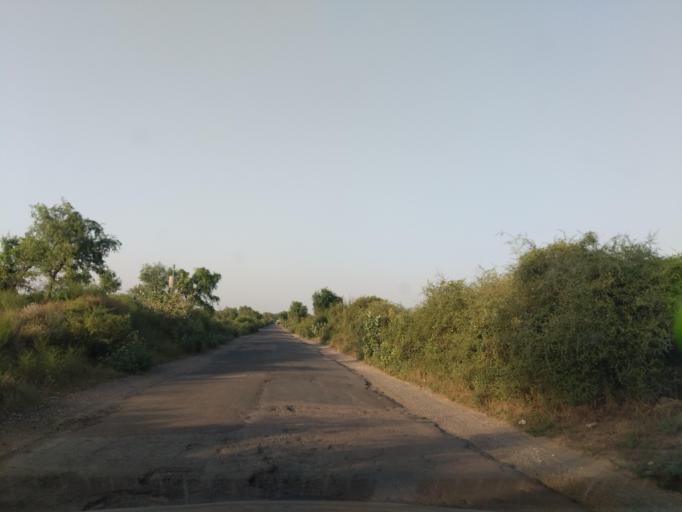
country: IN
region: Rajasthan
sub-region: Churu
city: Rajgarh
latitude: 28.5782
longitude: 75.3715
